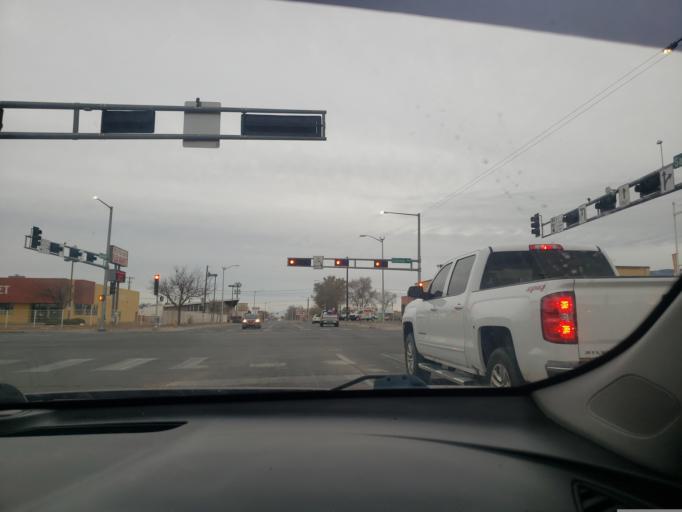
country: US
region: New Mexico
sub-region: Bernalillo County
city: Albuquerque
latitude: 35.0766
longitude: -106.5775
